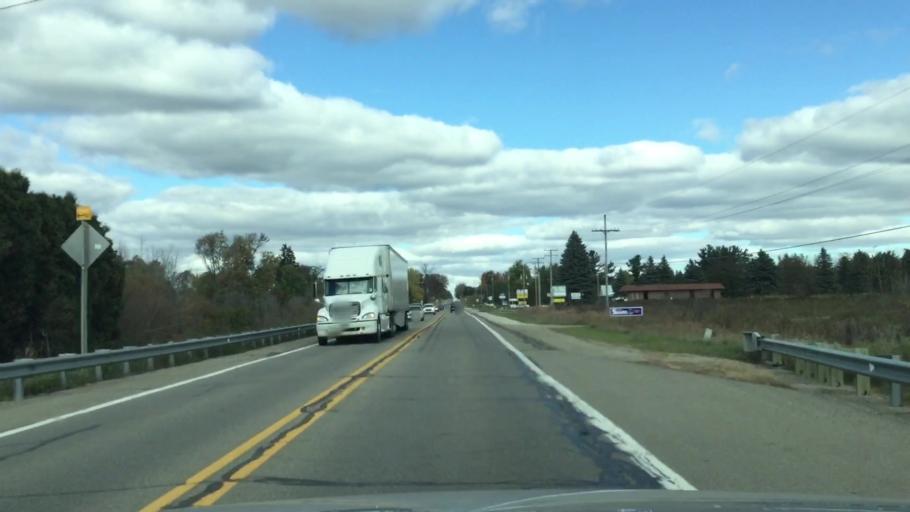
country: US
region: Michigan
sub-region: Lapeer County
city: Lapeer
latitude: 43.0919
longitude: -83.3077
